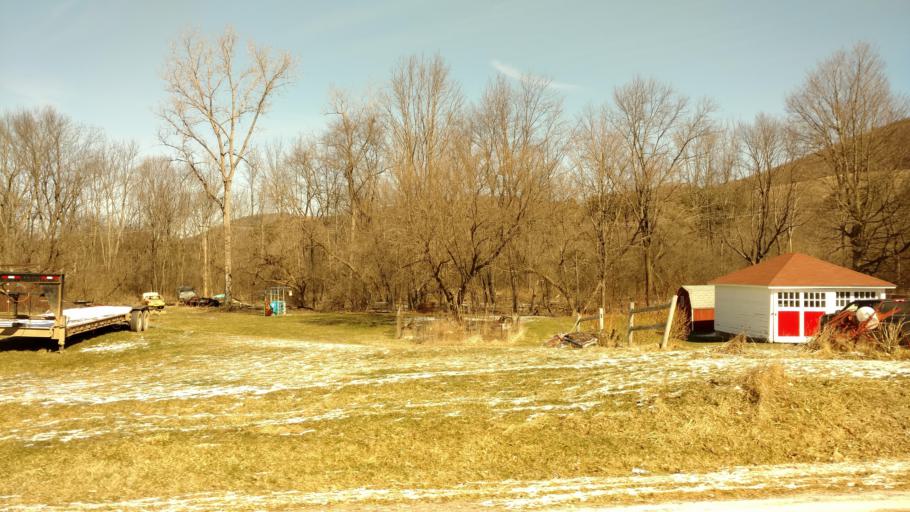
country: US
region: New York
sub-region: Allegany County
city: Wellsville
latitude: 42.0863
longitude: -77.9189
